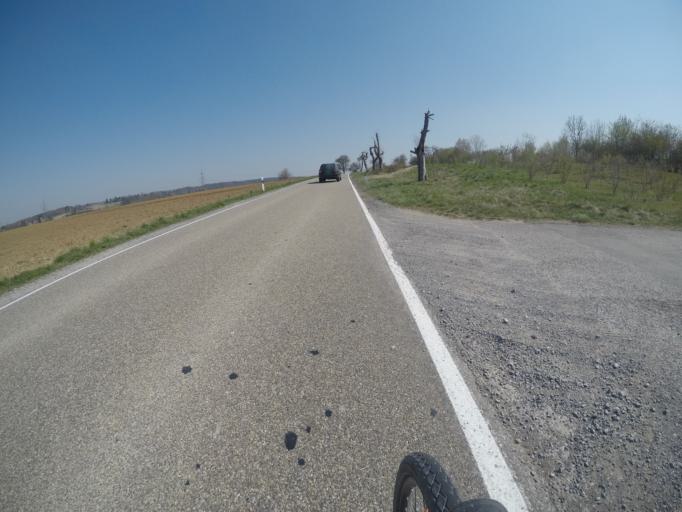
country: DE
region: Baden-Wuerttemberg
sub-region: Regierungsbezirk Stuttgart
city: Renningen
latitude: 48.7447
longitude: 8.9433
